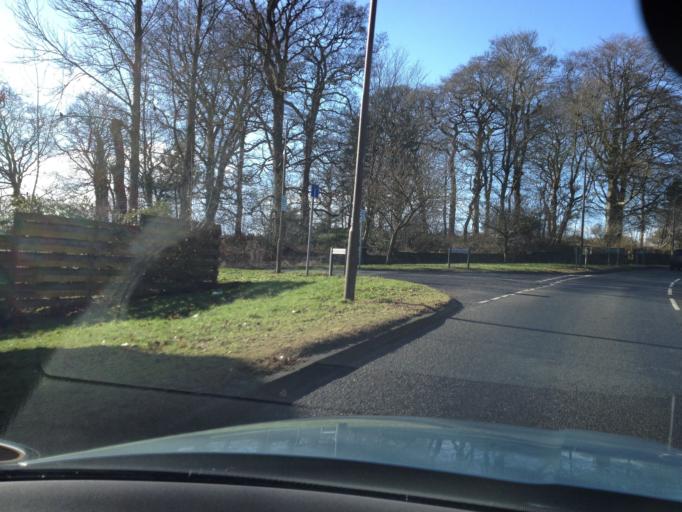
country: GB
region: Scotland
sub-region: West Lothian
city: Livingston
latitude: 55.8868
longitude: -3.5454
